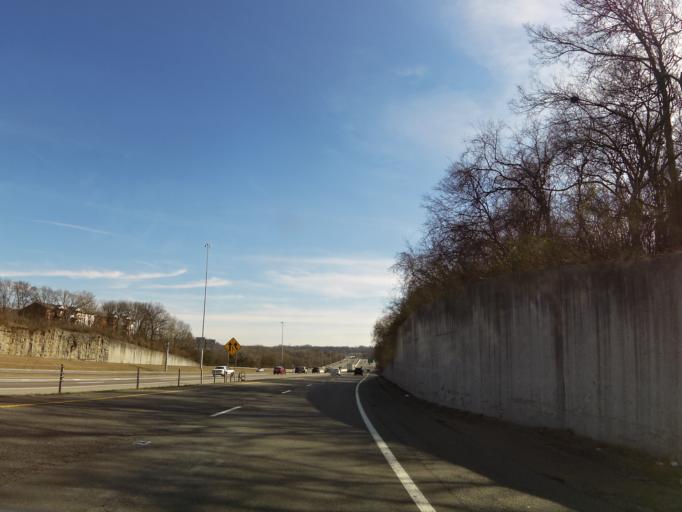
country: US
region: Tennessee
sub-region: Davidson County
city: Oak Hill
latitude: 36.1245
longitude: -86.7284
